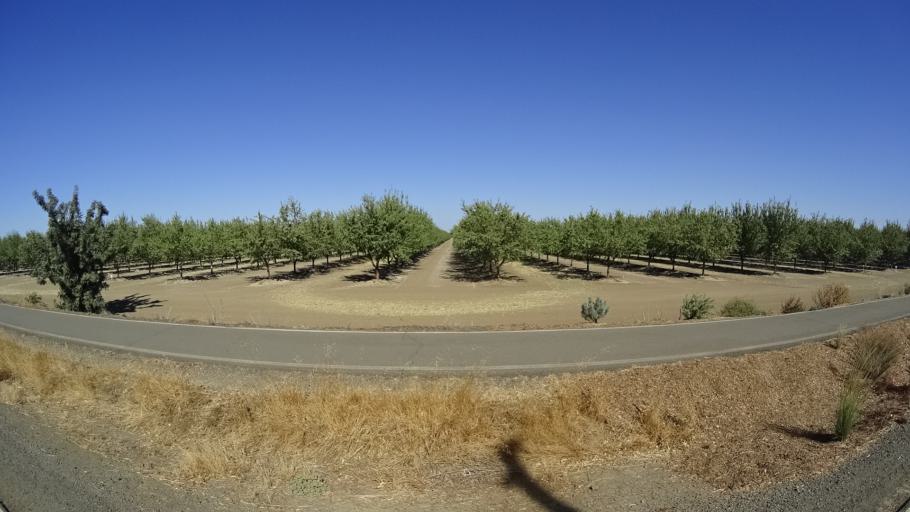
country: US
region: California
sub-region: Yolo County
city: Davis
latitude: 38.5470
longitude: -121.8230
